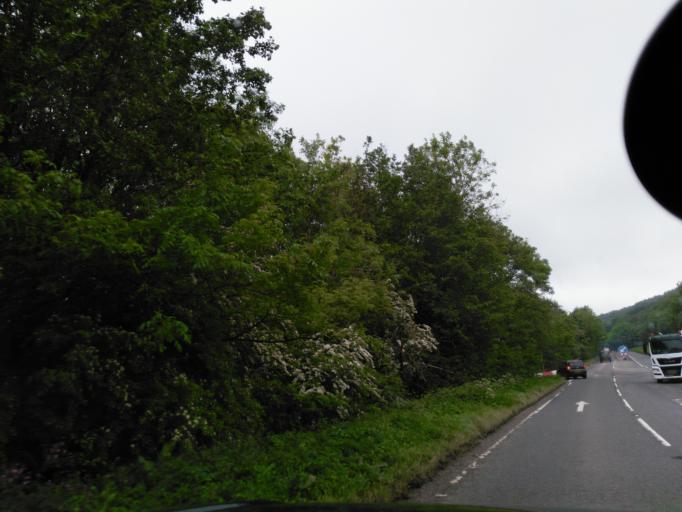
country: GB
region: England
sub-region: Somerset
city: Evercreech
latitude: 51.1912
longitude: -2.4407
